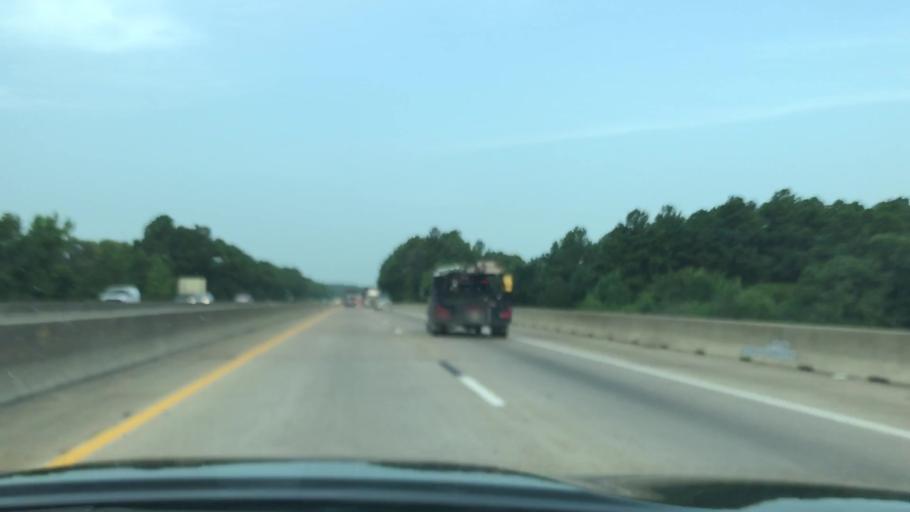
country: US
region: Texas
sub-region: Gregg County
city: Longview
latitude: 32.4382
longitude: -94.7430
